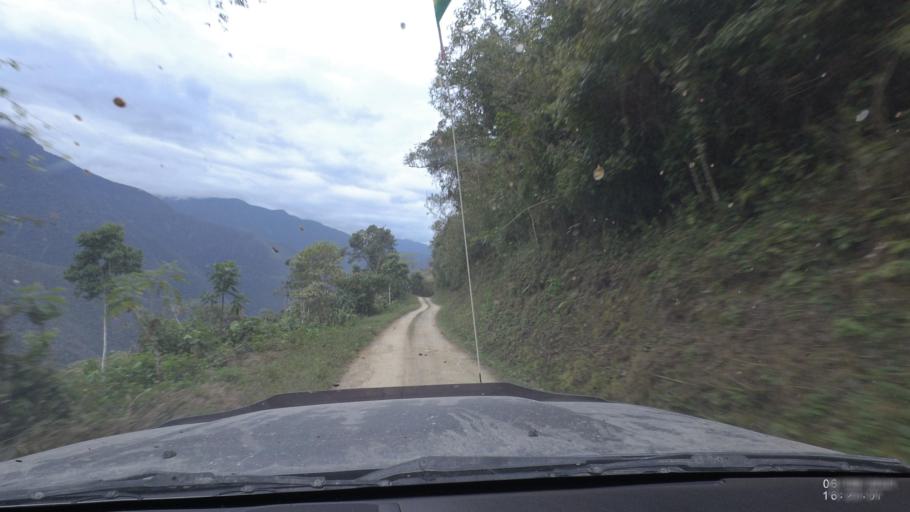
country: BO
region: La Paz
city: Quime
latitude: -16.5470
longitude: -66.7454
